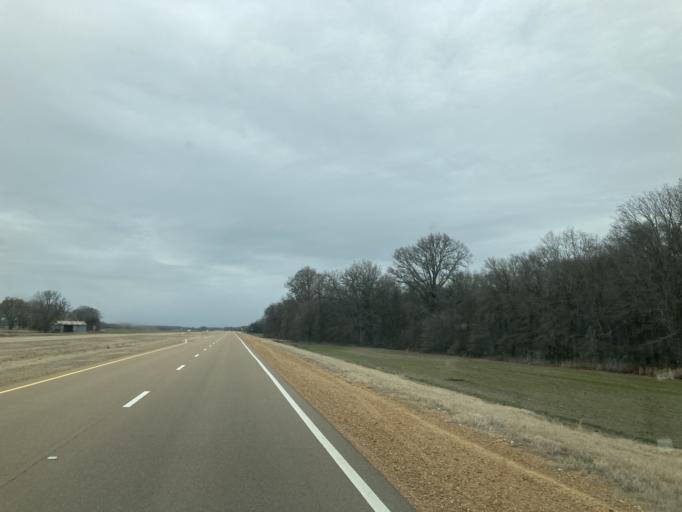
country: US
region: Mississippi
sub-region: Yazoo County
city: Yazoo City
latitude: 33.0075
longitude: -90.4696
